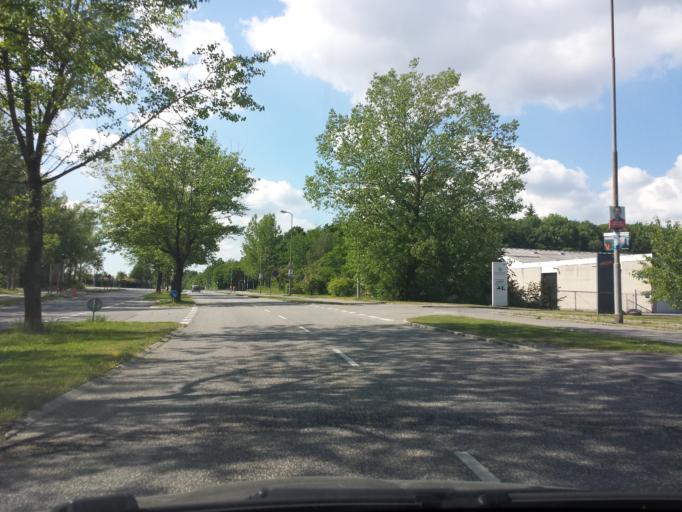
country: DK
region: Capital Region
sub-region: Herlev Kommune
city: Herlev
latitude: 55.6990
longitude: 12.4208
